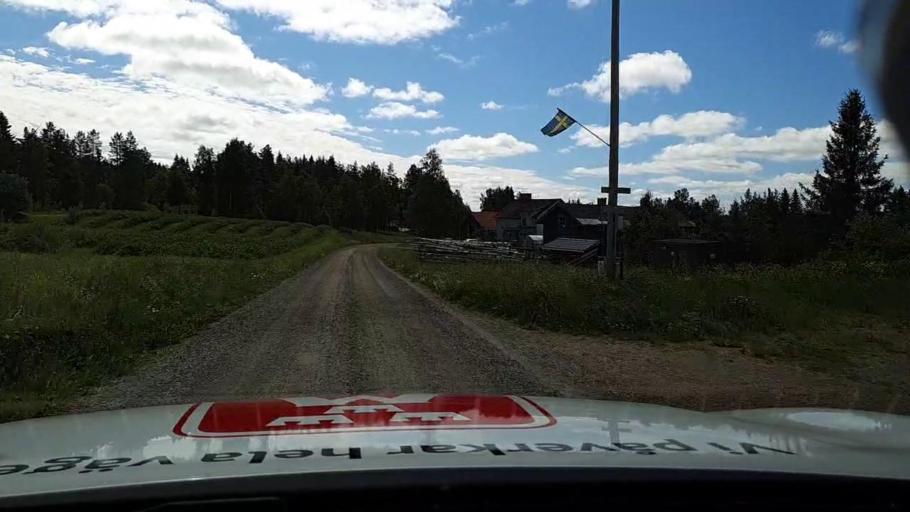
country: SE
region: Jaemtland
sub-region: Braecke Kommun
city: Braecke
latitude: 62.7636
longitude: 15.4989
